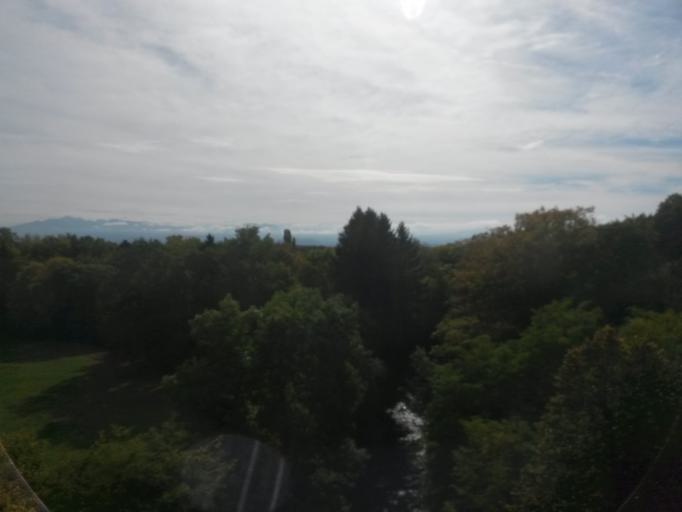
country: CH
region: Vaud
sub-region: Morges District
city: Aubonne
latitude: 46.4766
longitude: 6.4067
